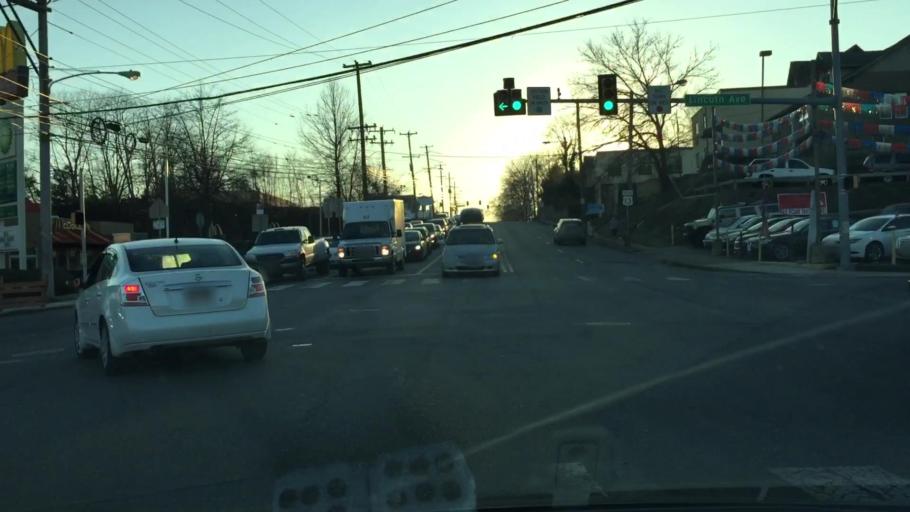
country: US
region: Pennsylvania
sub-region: Delaware County
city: Prospect Park
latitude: 39.8825
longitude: -75.3058
